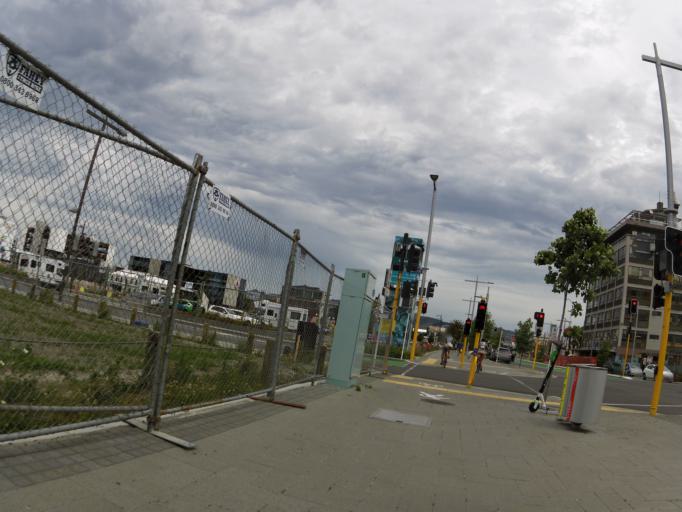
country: NZ
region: Canterbury
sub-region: Christchurch City
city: Christchurch
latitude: -43.5329
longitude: 172.6398
